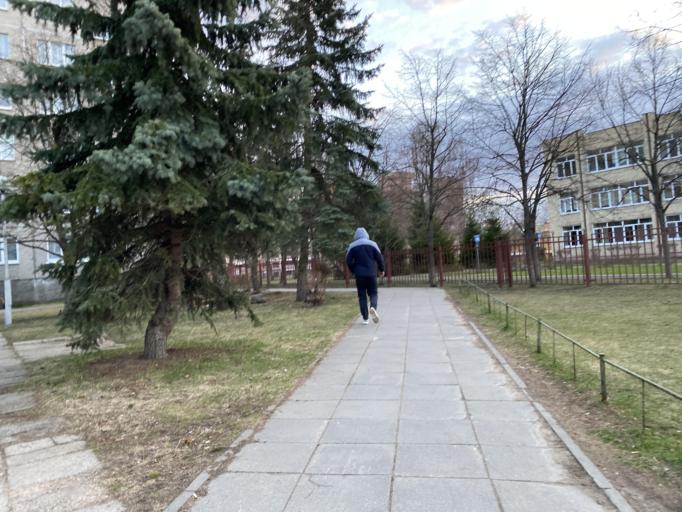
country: BY
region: Minsk
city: Bal'shavik
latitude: 53.9582
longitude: 27.6194
